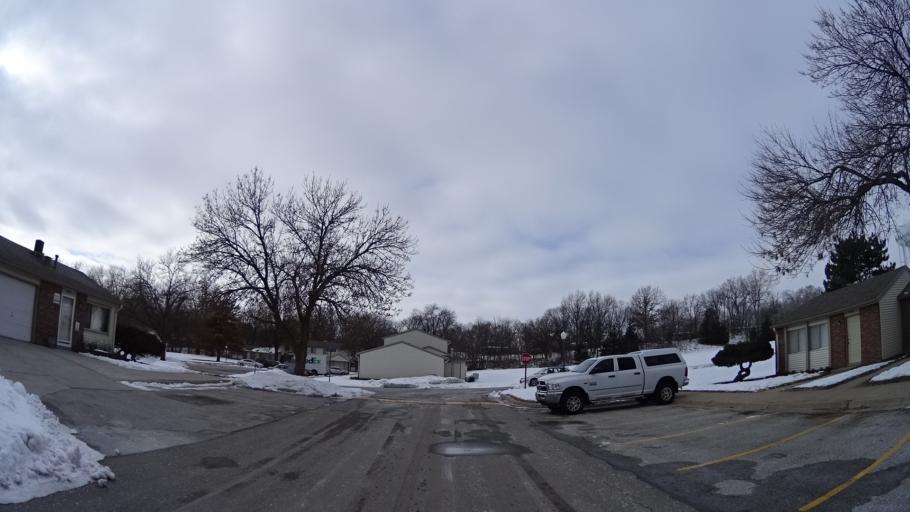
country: US
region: Nebraska
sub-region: Sarpy County
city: Offutt Air Force Base
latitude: 41.1192
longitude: -95.9554
